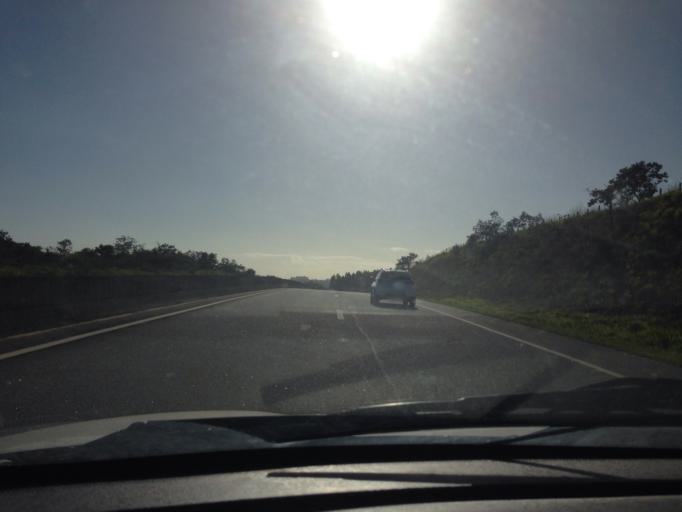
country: BR
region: Espirito Santo
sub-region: Guarapari
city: Guarapari
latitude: -20.6262
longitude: -40.4995
